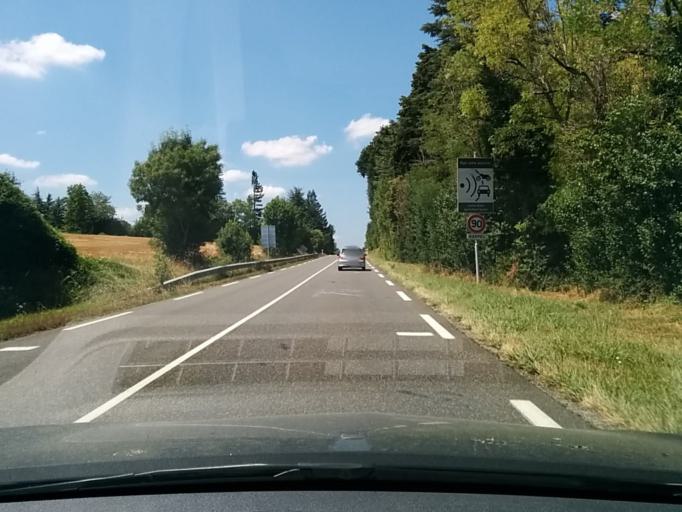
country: FR
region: Midi-Pyrenees
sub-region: Departement du Gers
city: Vic-Fezensac
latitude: 43.7476
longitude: 0.3389
